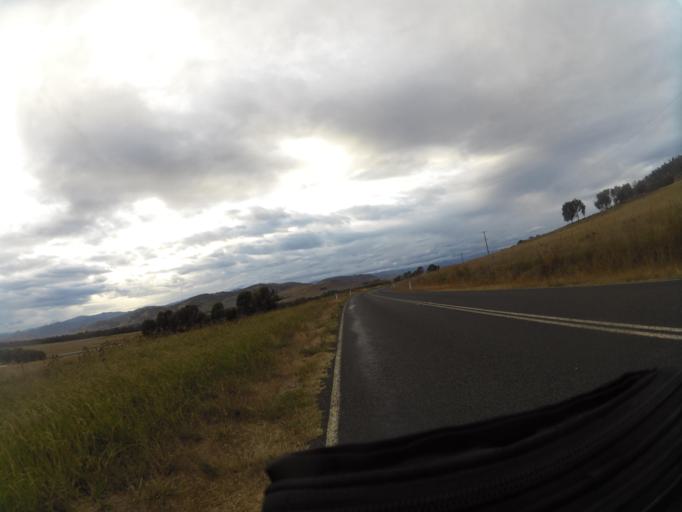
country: AU
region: New South Wales
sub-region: Snowy River
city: Jindabyne
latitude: -36.0752
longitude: 147.9705
